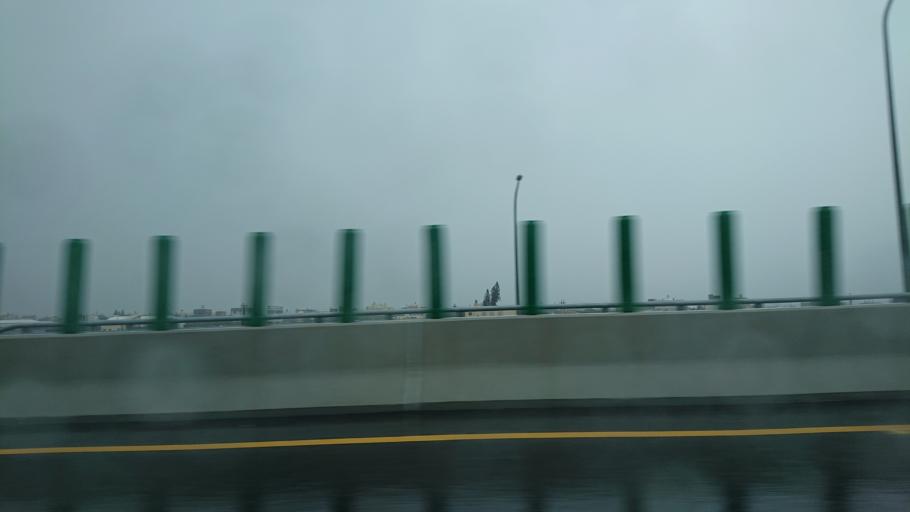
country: TW
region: Taiwan
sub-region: Changhua
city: Chang-hua
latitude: 23.9403
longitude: 120.3228
